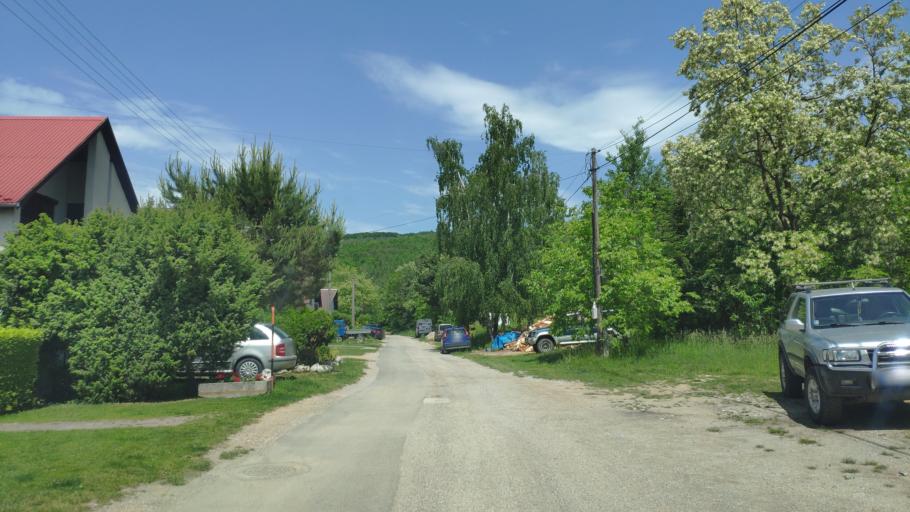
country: SK
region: Kosicky
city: Medzev
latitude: 48.7176
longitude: 20.9708
